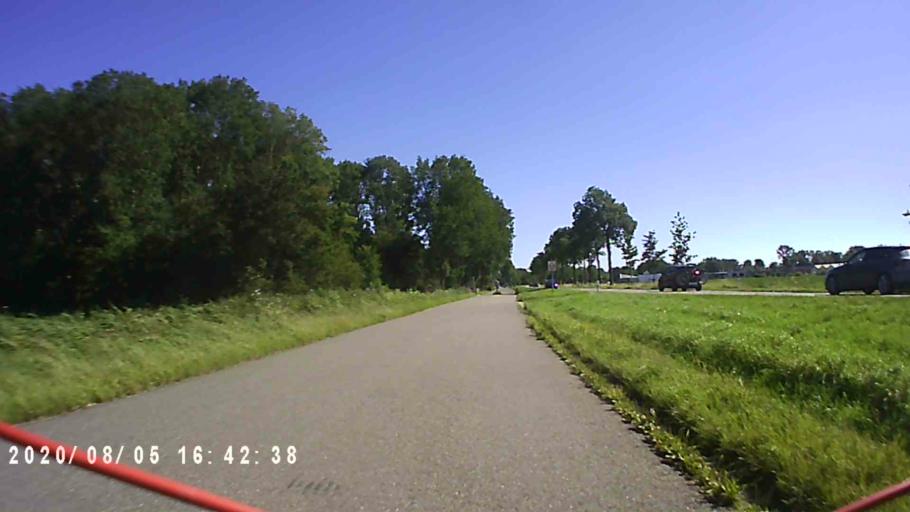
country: NL
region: Groningen
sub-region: Gemeente Winsum
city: Winsum
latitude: 53.3387
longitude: 6.5110
